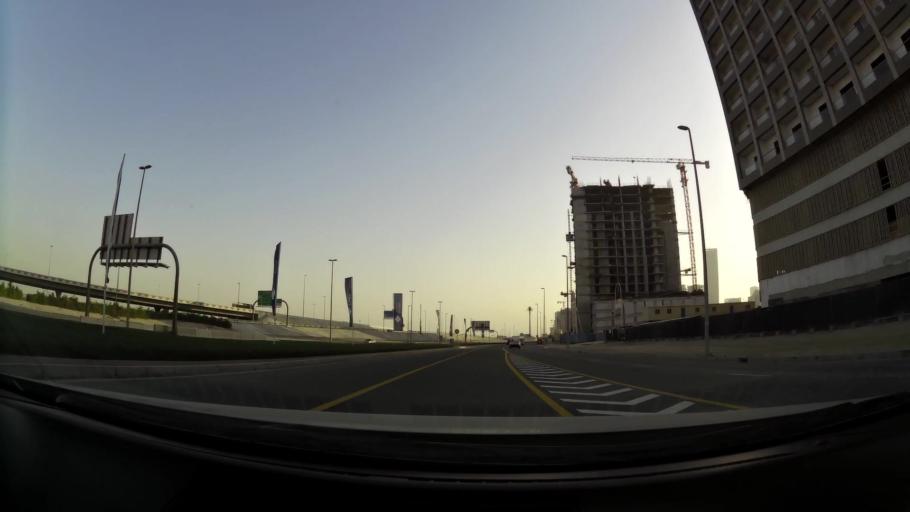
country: AE
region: Dubai
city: Dubai
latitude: 25.1839
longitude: 55.2851
